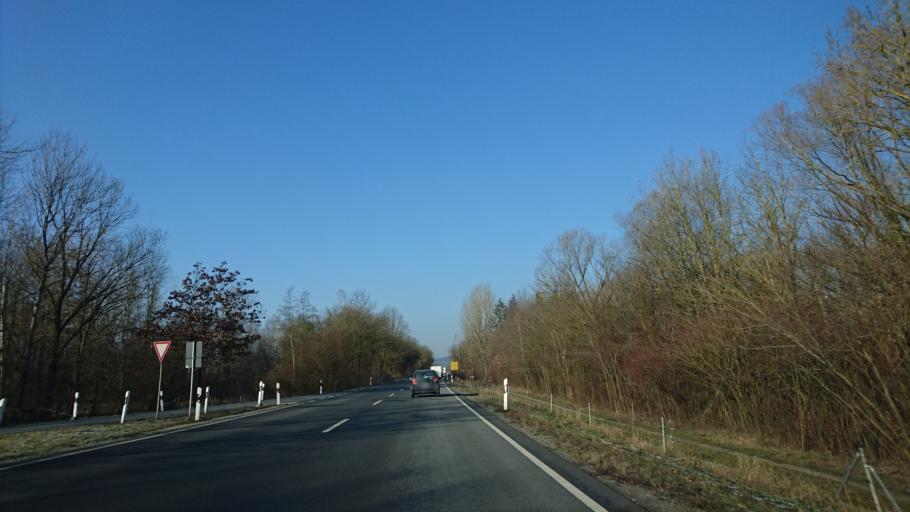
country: DE
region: Bavaria
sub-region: Lower Bavaria
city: Bad Birnbach
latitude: 48.4352
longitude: 13.0773
